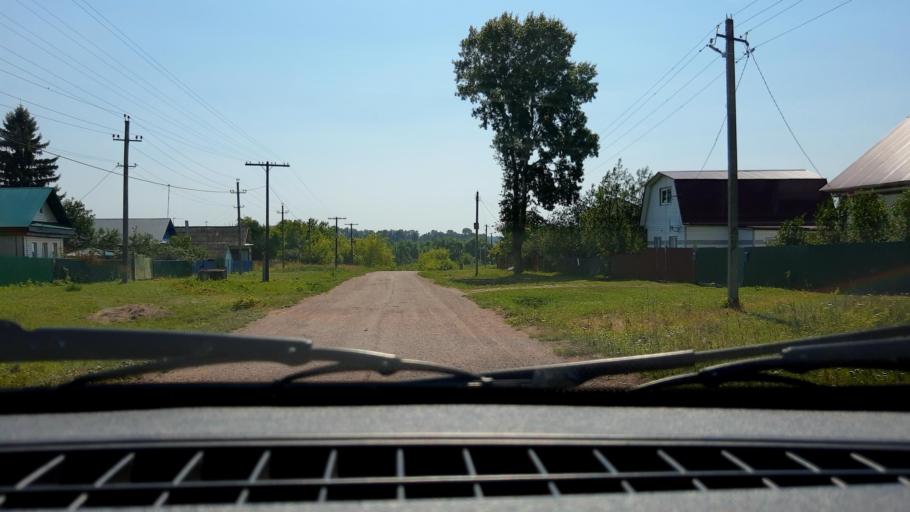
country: RU
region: Bashkortostan
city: Kushnarenkovo
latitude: 55.0705
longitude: 55.1655
